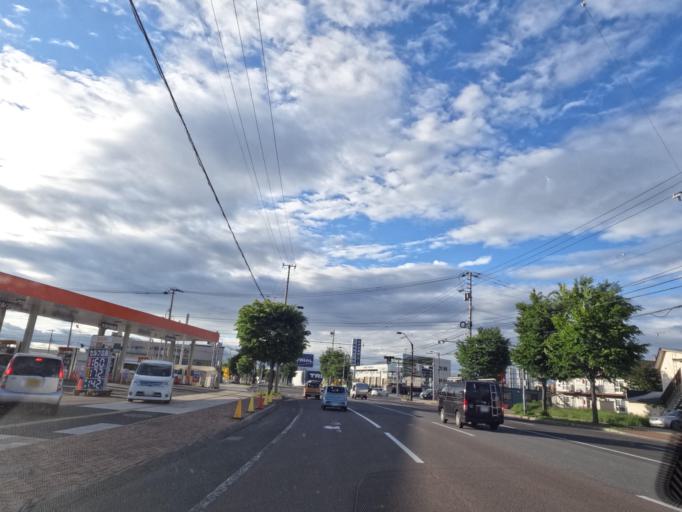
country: JP
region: Hokkaido
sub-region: Asahikawa-shi
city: Asahikawa
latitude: 43.7477
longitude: 142.3579
